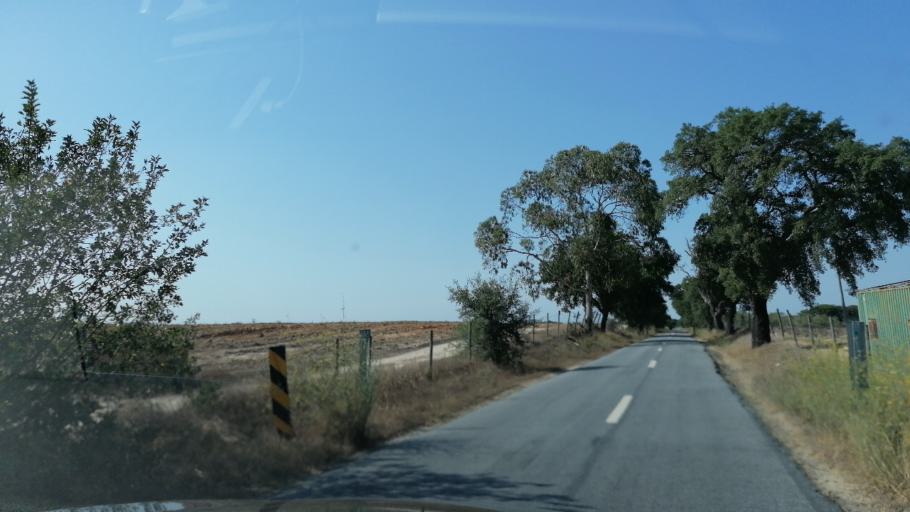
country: PT
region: Evora
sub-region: Vendas Novas
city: Vendas Novas
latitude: 38.7298
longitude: -8.6229
